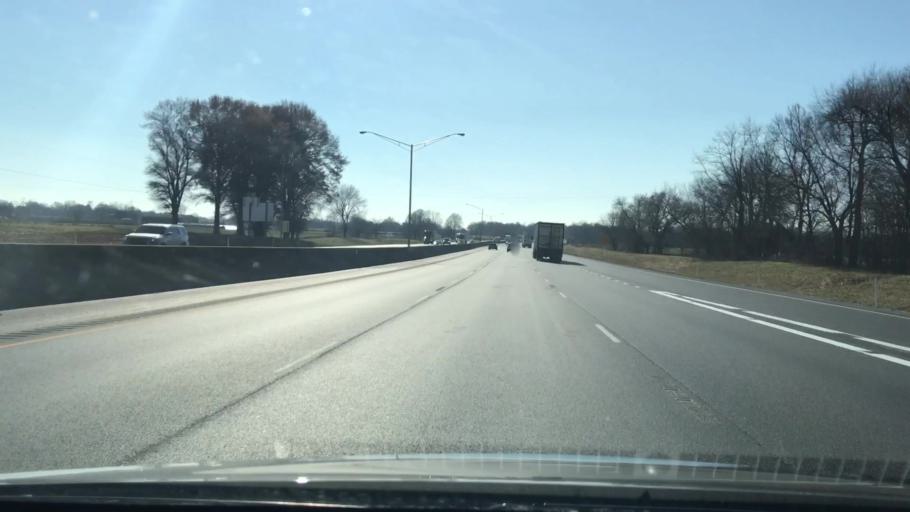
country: US
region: Kentucky
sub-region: Edmonson County
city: Brownsville
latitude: 37.0281
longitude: -86.2423
